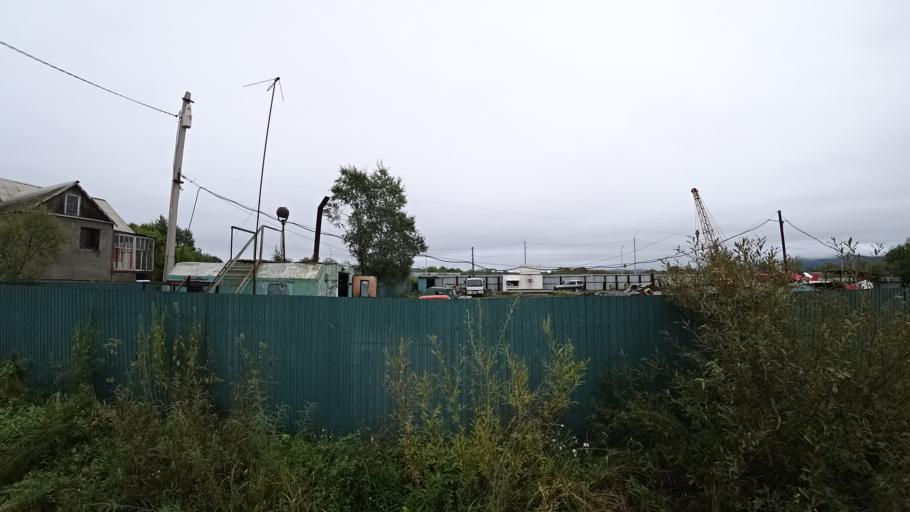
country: RU
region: Primorskiy
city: Monastyrishche
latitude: 44.1999
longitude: 132.4472
